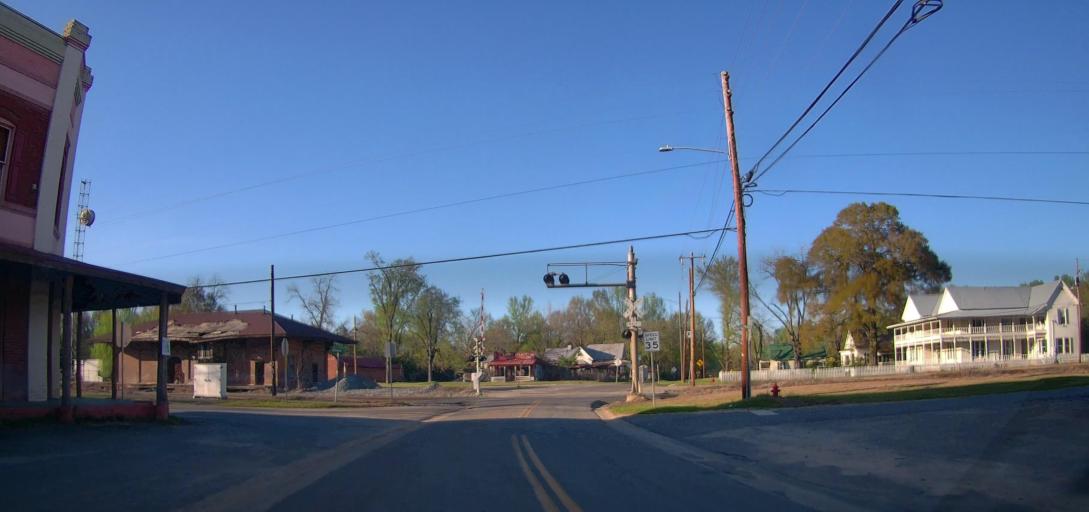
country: US
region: Georgia
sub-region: Wilkinson County
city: Irwinton
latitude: 32.8265
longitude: -83.0801
